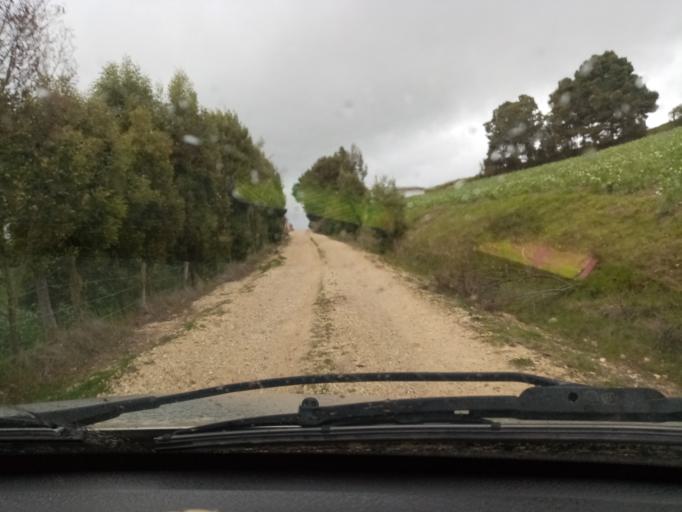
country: CO
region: Boyaca
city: Siachoque
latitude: 5.5523
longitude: -73.2495
